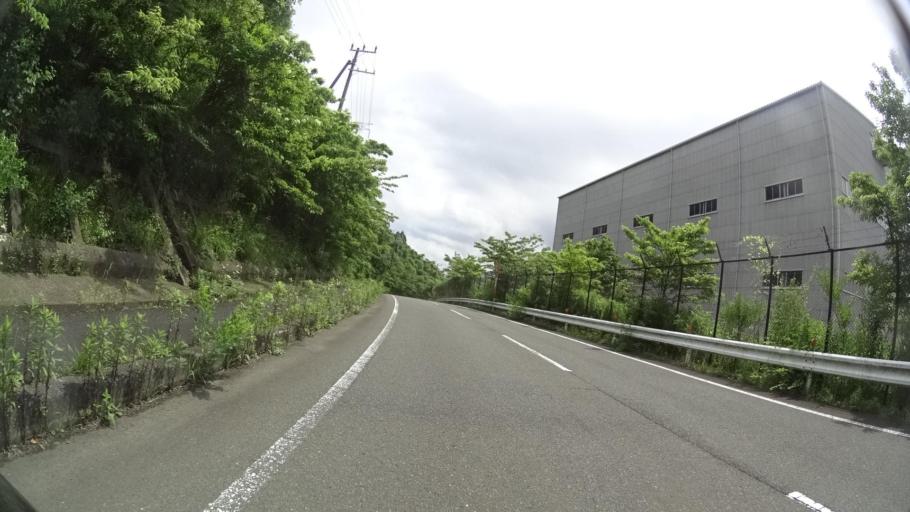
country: JP
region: Kyoto
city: Maizuru
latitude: 35.5301
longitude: 135.3463
